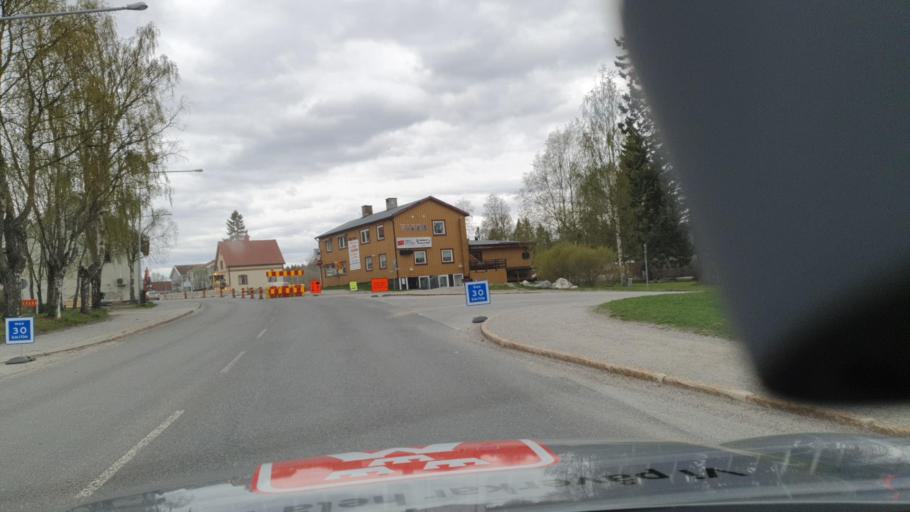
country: SE
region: Vaesternorrland
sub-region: OErnskoeldsviks Kommun
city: Ornskoldsvik
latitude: 63.2644
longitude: 18.6872
